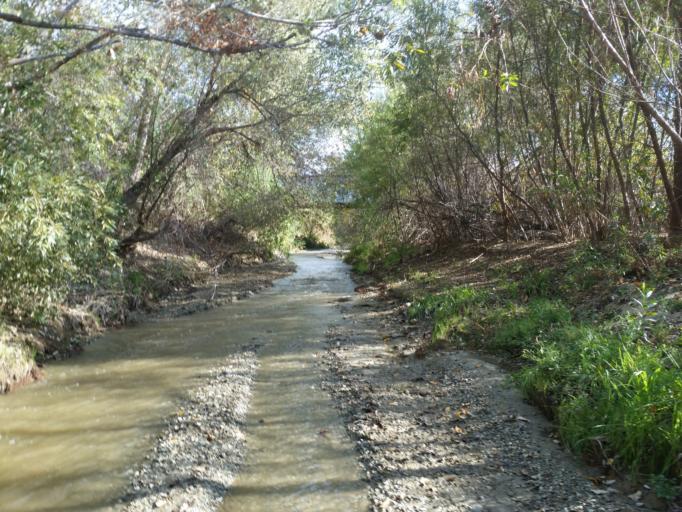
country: US
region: California
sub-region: San Bernardino County
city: Redlands
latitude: 34.0148
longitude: -117.1798
